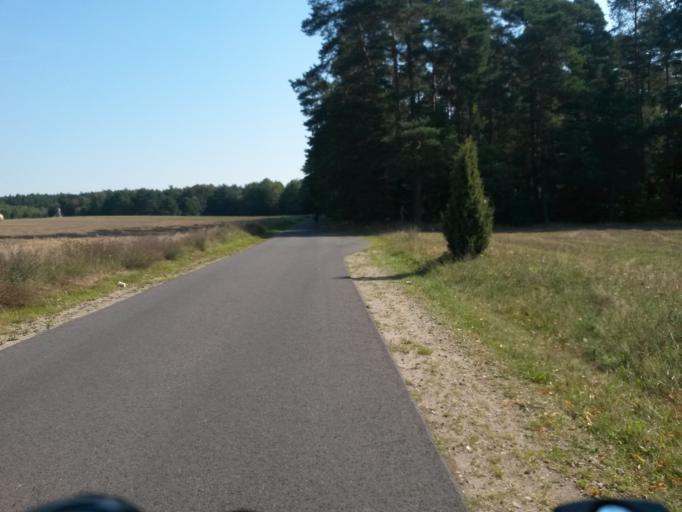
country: DE
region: Brandenburg
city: Templin
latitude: 53.0455
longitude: 13.5041
